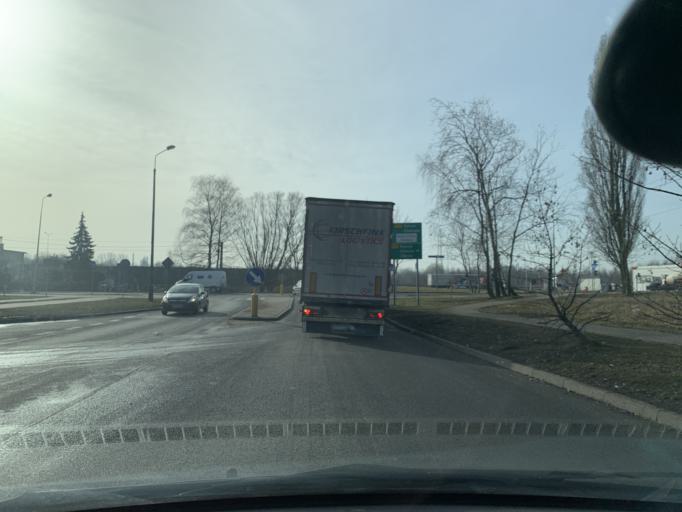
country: PL
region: Silesian Voivodeship
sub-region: Ruda Slaska
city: Ruda Slaska
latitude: 50.3015
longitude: 18.8683
